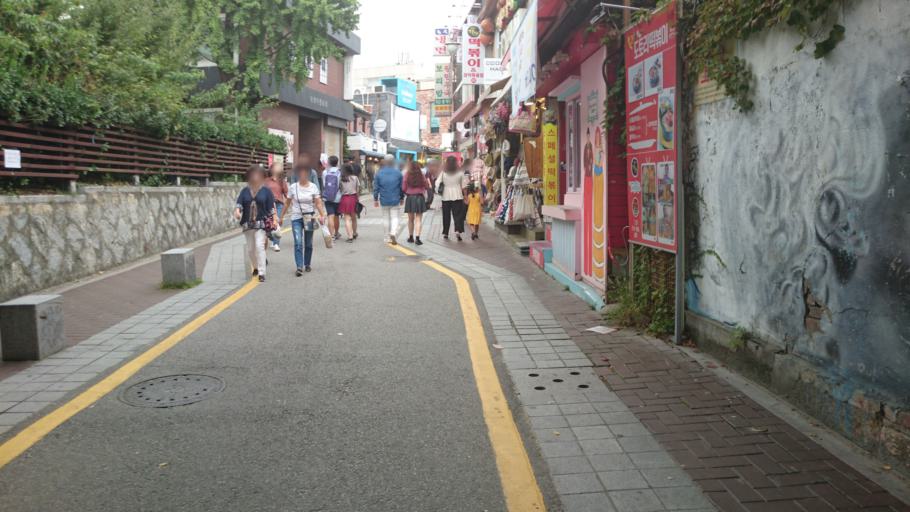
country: KR
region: Seoul
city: Seoul
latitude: 37.5783
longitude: 126.9822
